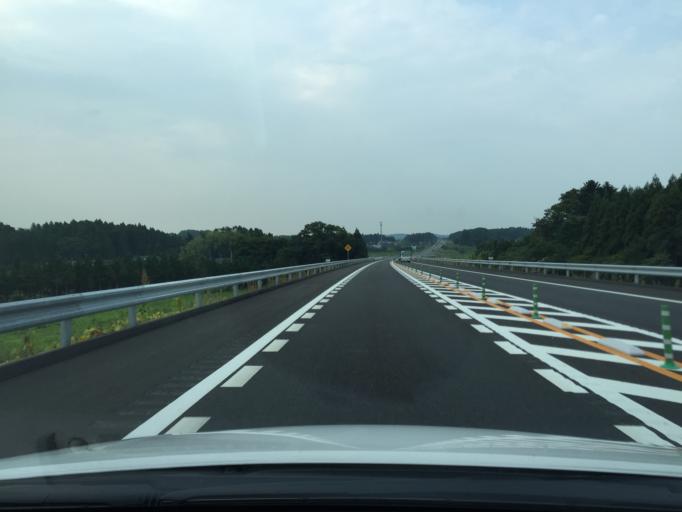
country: JP
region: Fukushima
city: Namie
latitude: 37.5390
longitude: 140.9408
